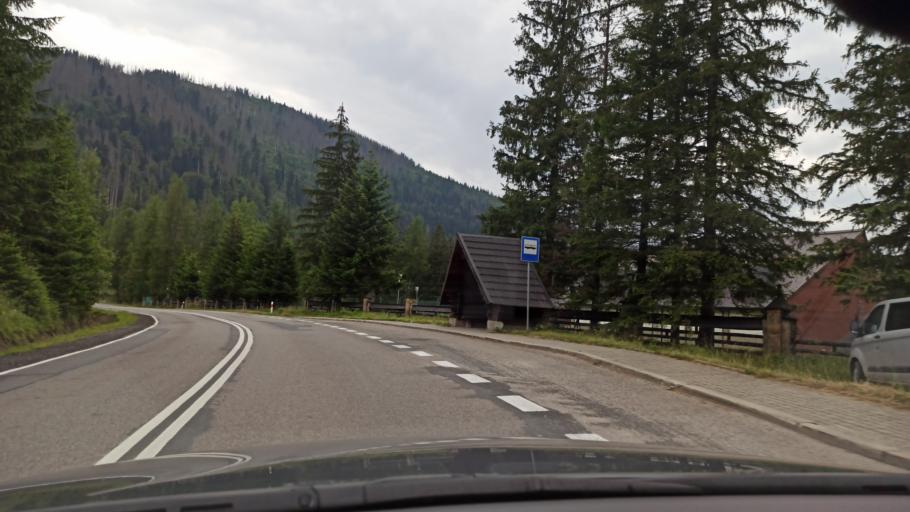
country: PL
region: Lesser Poland Voivodeship
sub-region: Powiat tatrzanski
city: Koscielisko
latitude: 49.2775
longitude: 19.9004
